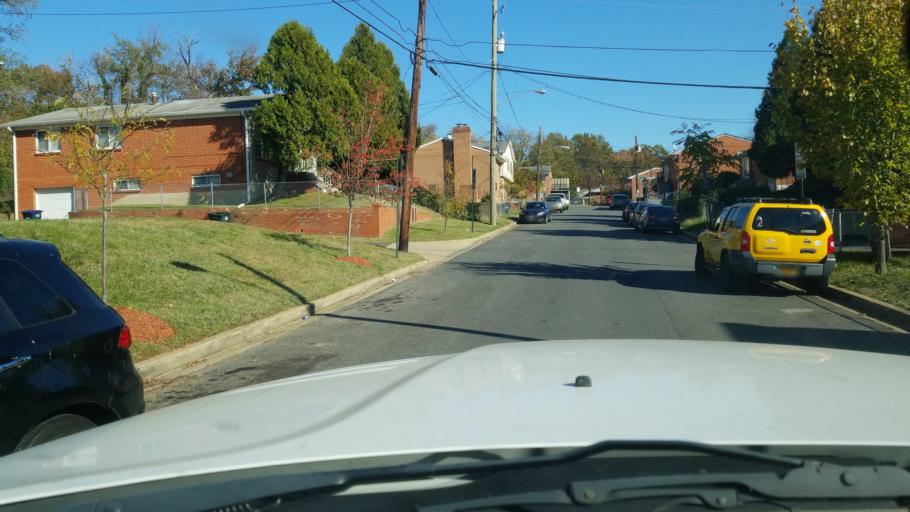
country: US
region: Maryland
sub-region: Prince George's County
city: Capitol Heights
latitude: 38.8926
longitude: -76.9390
